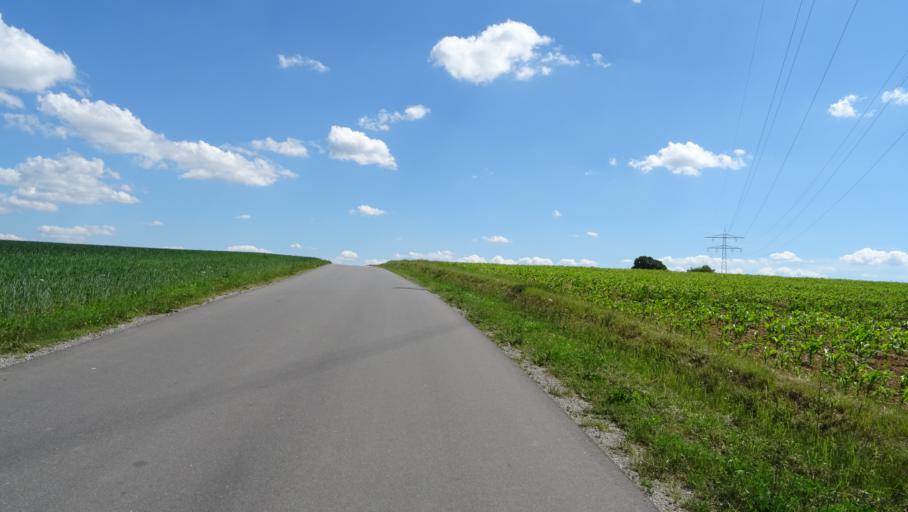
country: DE
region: Baden-Wuerttemberg
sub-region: Karlsruhe Region
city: Adelsheim
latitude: 49.3998
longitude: 9.3671
